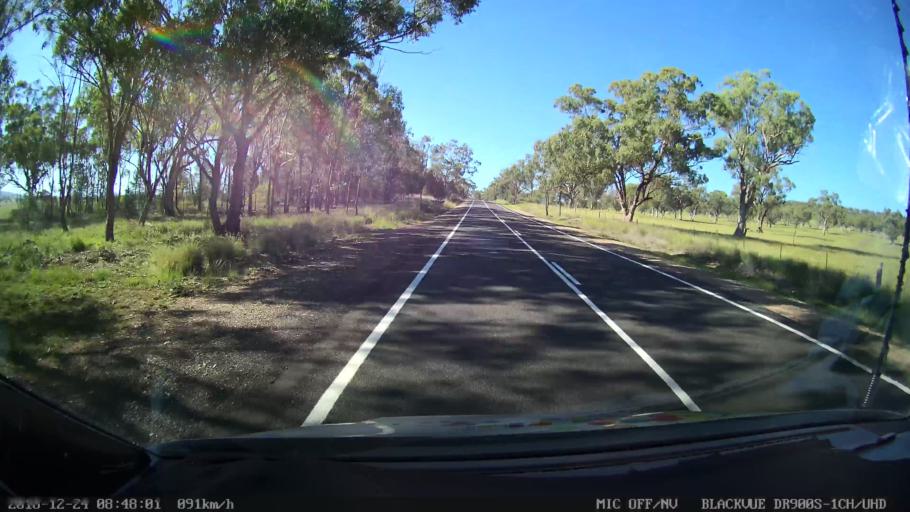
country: AU
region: New South Wales
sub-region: Liverpool Plains
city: Quirindi
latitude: -31.4498
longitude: 150.6462
